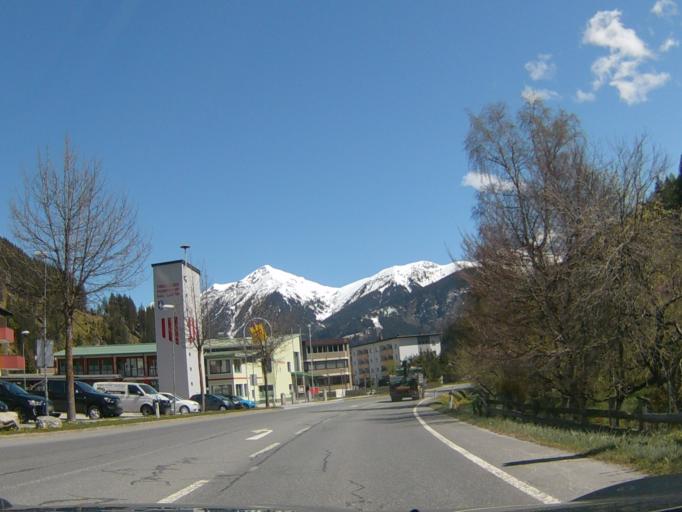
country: AT
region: Salzburg
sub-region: Politischer Bezirk Sankt Johann im Pongau
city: Bad Gastein
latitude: 47.1003
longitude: 13.1270
